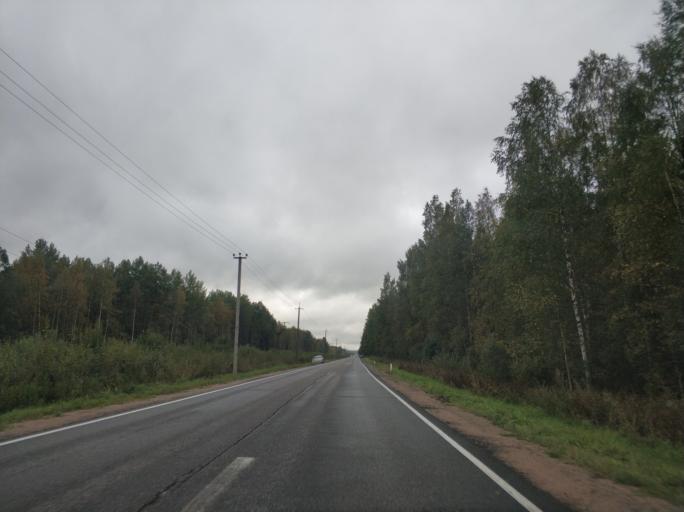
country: RU
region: Leningrad
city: Borisova Griva
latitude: 60.1137
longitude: 30.9631
